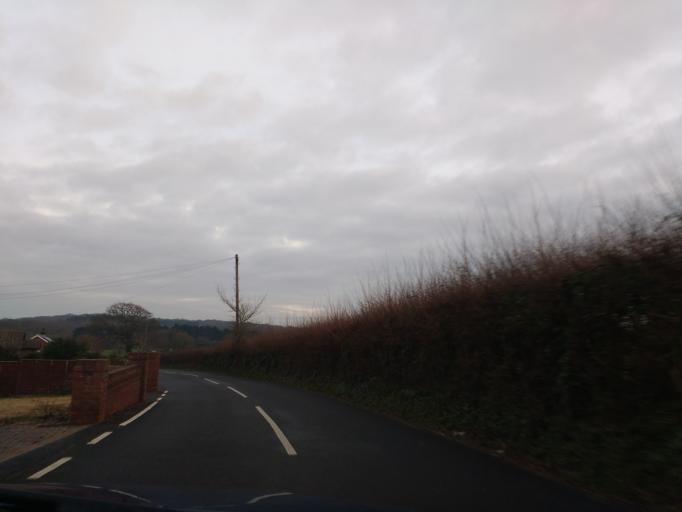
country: GB
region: England
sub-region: Isle of Wight
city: Northwood
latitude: 50.7251
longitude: -1.3558
